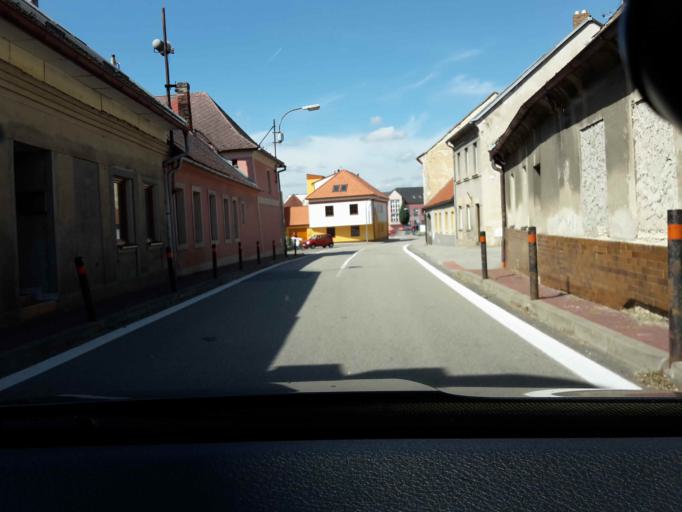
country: CZ
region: Jihocesky
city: Kardasova Recice
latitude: 49.1835
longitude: 14.8548
